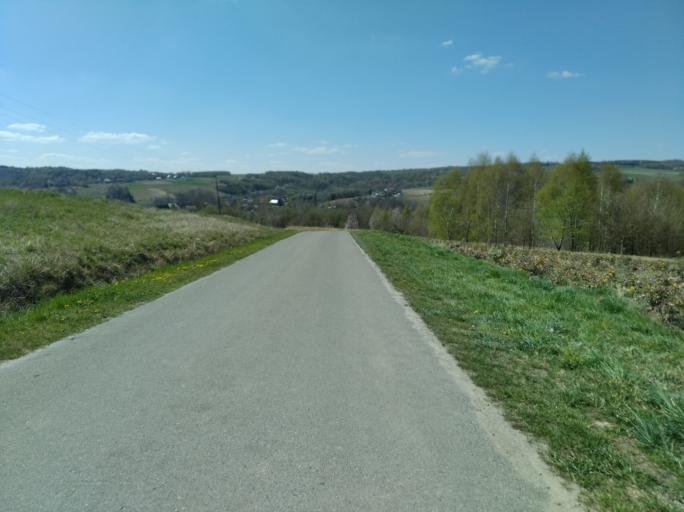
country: PL
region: Subcarpathian Voivodeship
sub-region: Powiat strzyzowski
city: Wisniowa
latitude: 49.9176
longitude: 21.6762
